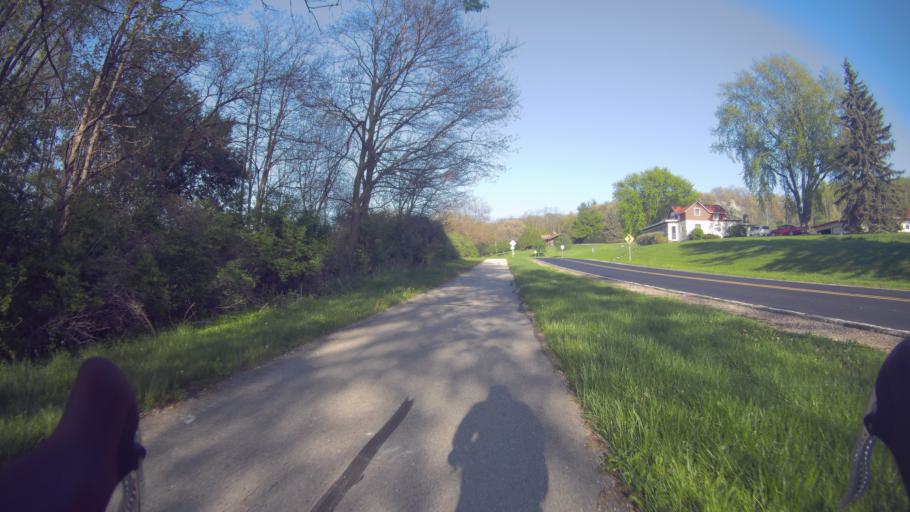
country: US
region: Wisconsin
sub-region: Dane County
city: Madison
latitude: 43.0232
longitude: -89.3786
